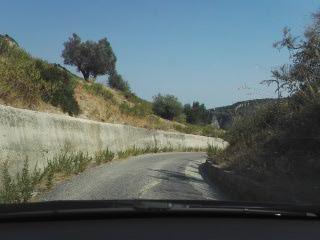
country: IT
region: Calabria
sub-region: Provincia di Reggio Calabria
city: Camini
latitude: 38.4453
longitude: 16.4708
